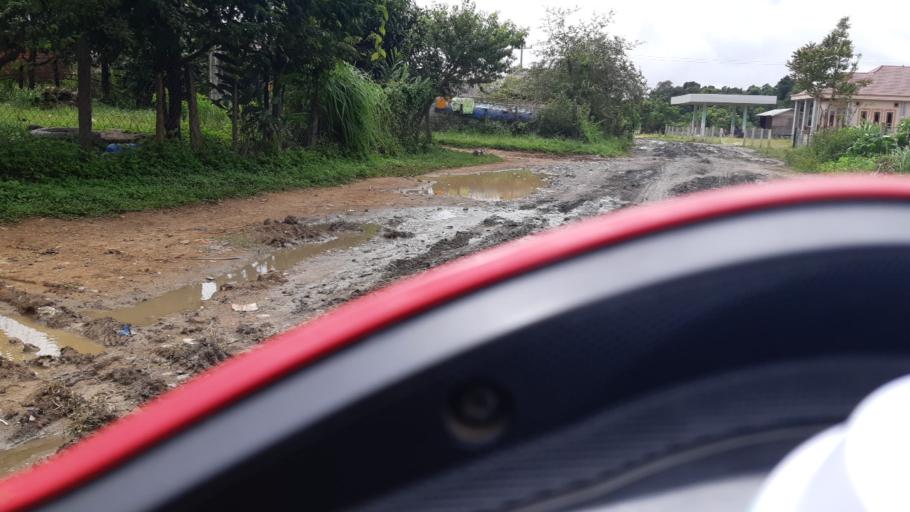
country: LA
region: Loungnamtha
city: Muang Nale
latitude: 20.0145
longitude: 101.5177
